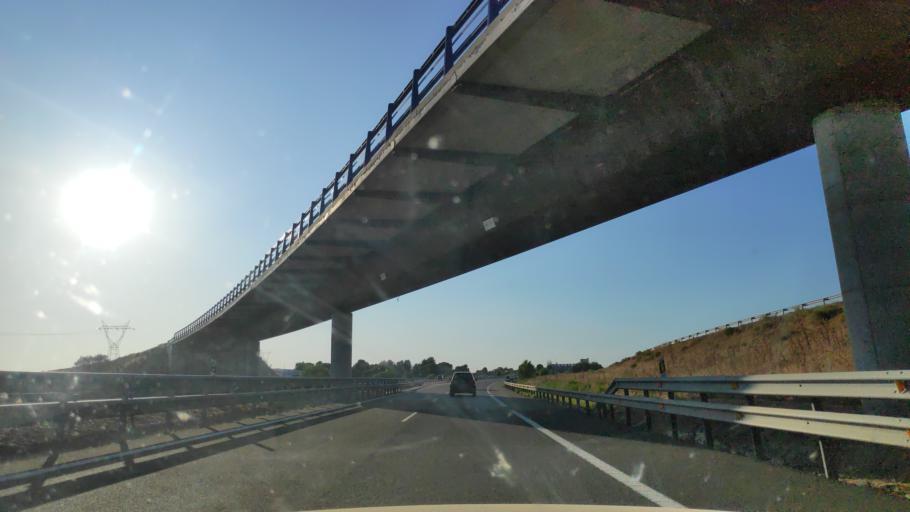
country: ES
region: Castille-La Mancha
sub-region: Provincia de Cuenca
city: Tarancon
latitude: 39.9996
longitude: -3.0216
